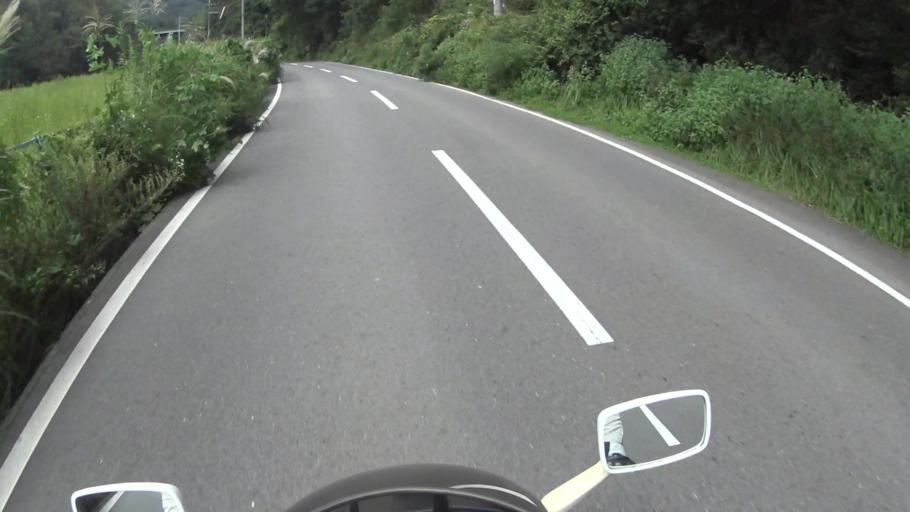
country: JP
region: Kyoto
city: Uji
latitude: 34.9168
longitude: 135.8859
